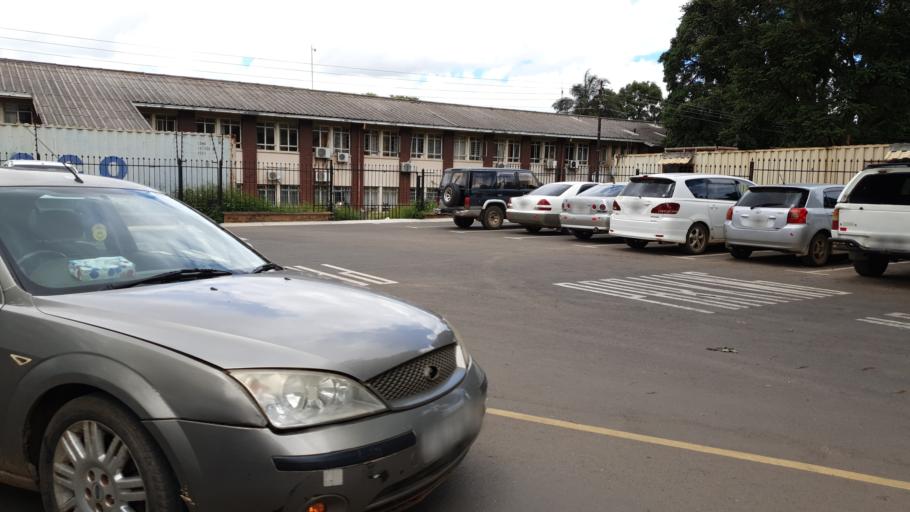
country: ZM
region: Lusaka
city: Lusaka
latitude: -15.4250
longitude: 28.3096
